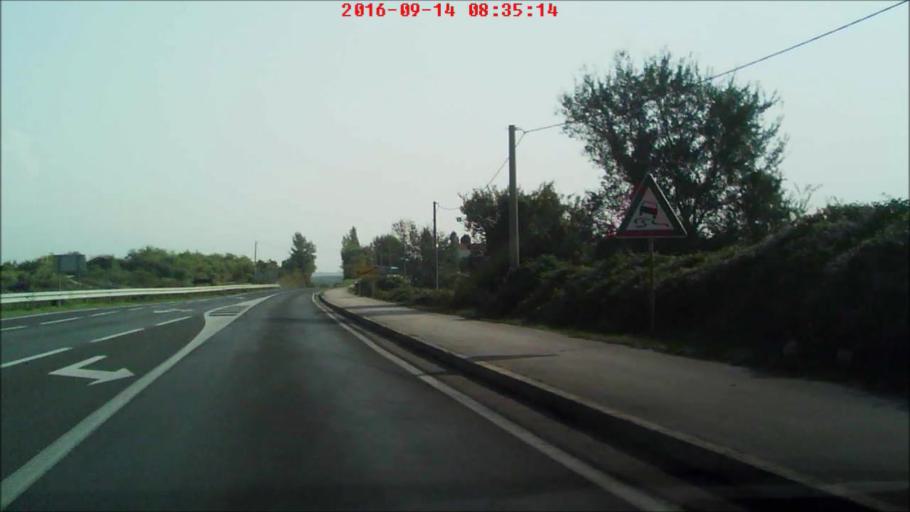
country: HR
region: Zadarska
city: Policnik
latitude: 44.1485
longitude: 15.3268
